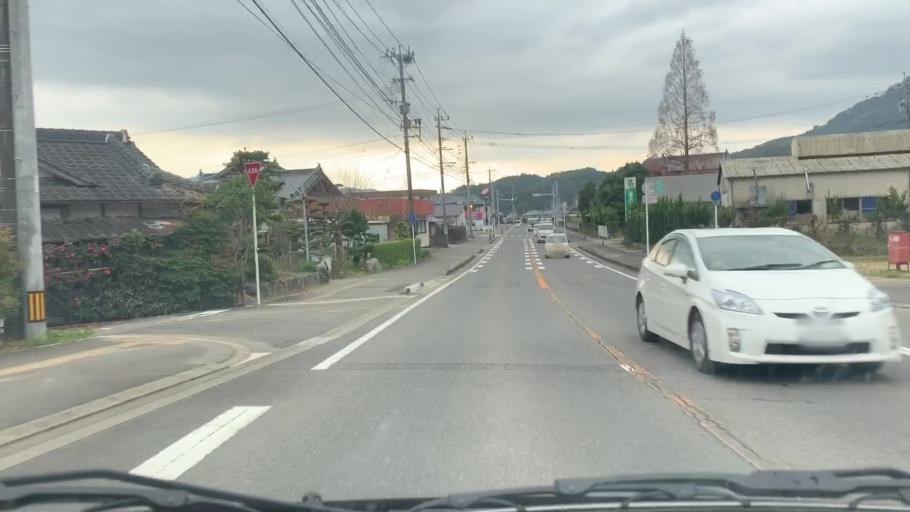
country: JP
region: Saga Prefecture
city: Takeocho-takeo
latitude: 33.1743
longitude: 130.0485
